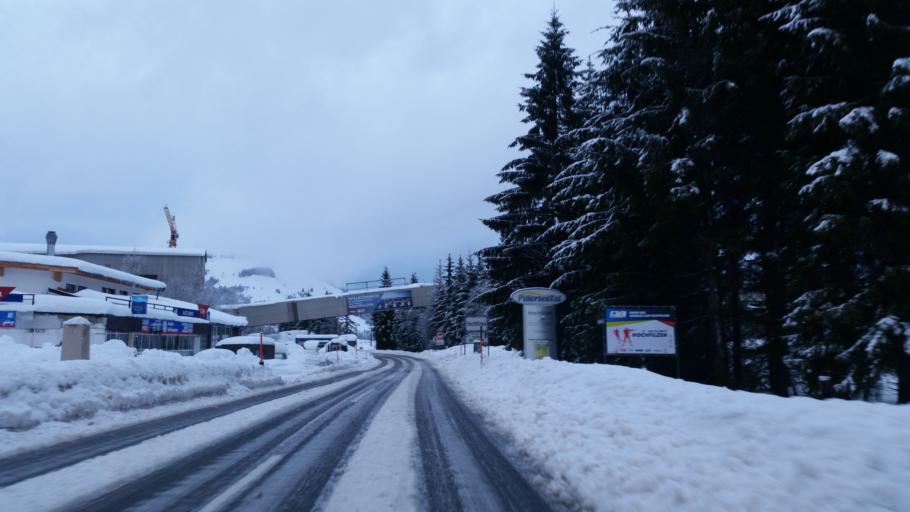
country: AT
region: Tyrol
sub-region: Politischer Bezirk Kitzbuhel
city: Hochfilzen
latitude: 47.4635
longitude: 12.6324
